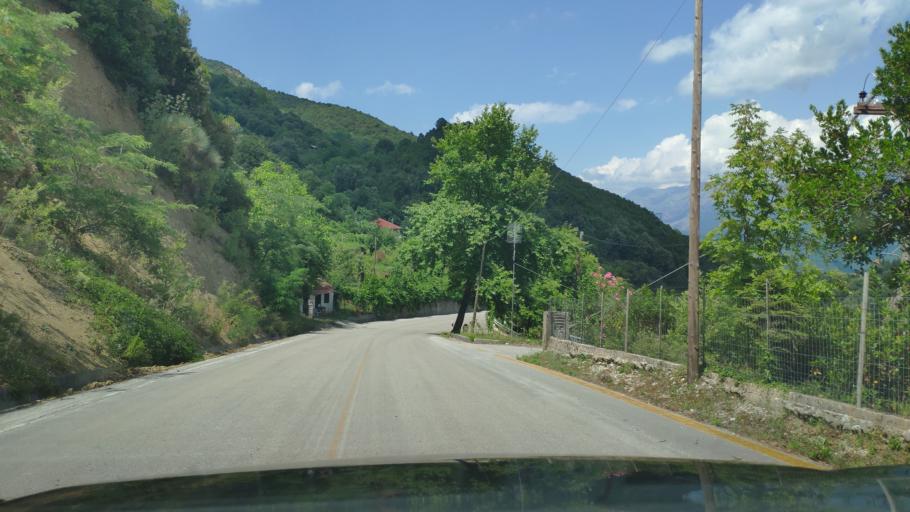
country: GR
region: Epirus
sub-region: Nomos Artas
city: Agios Dimitrios
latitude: 39.3517
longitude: 21.0154
